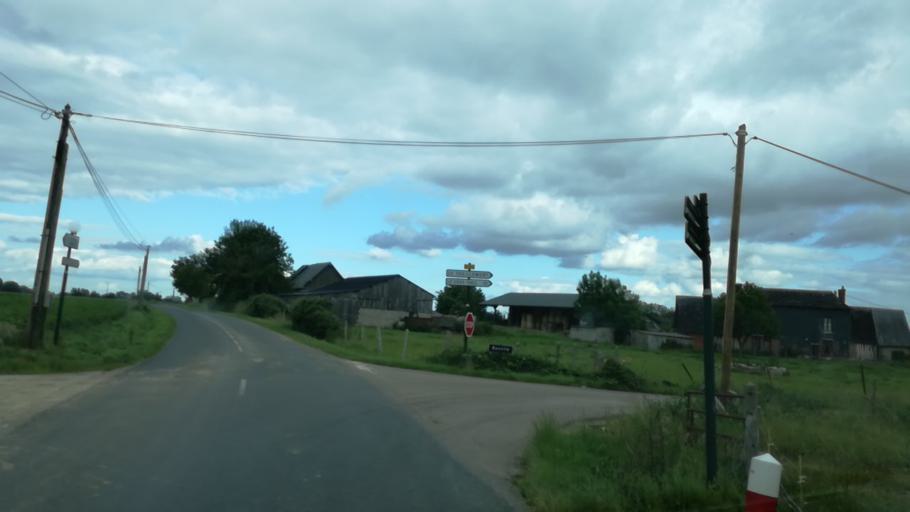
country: FR
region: Haute-Normandie
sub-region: Departement de l'Eure
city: Bourg-Achard
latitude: 49.3012
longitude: 0.8028
